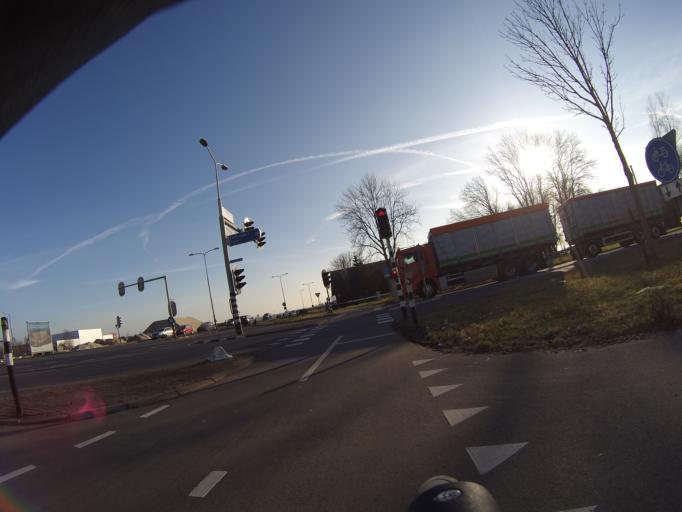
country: NL
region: Utrecht
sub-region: Gemeente Bunschoten
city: Bunschoten
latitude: 52.2272
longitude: 5.3699
